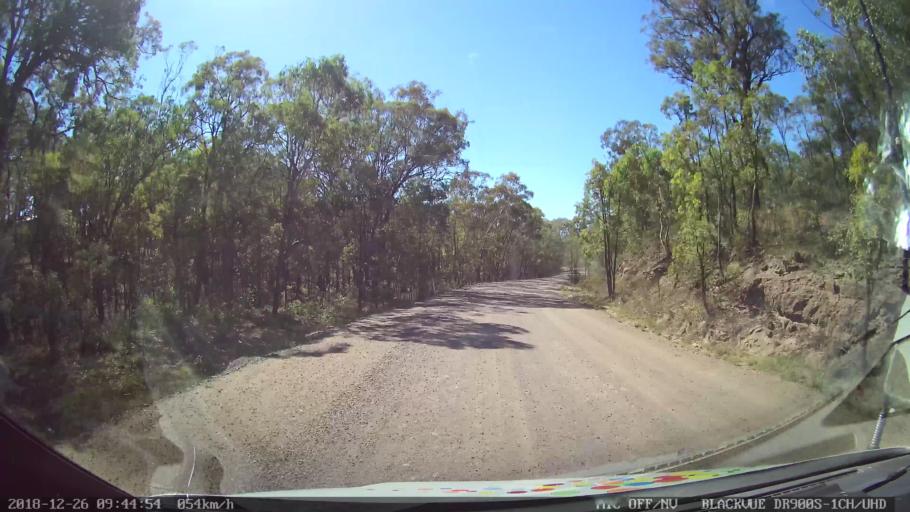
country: AU
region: New South Wales
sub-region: Mid-Western Regional
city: Kandos
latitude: -32.9597
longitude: 150.0995
